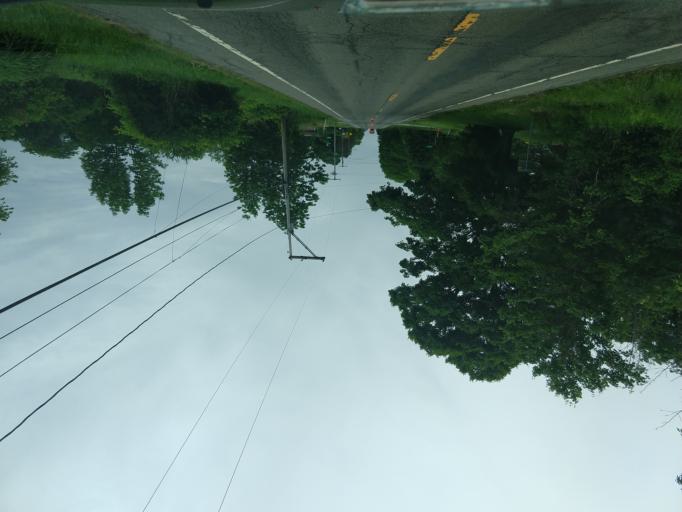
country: US
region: New York
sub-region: Tompkins County
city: Dryden
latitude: 42.4911
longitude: -76.2795
